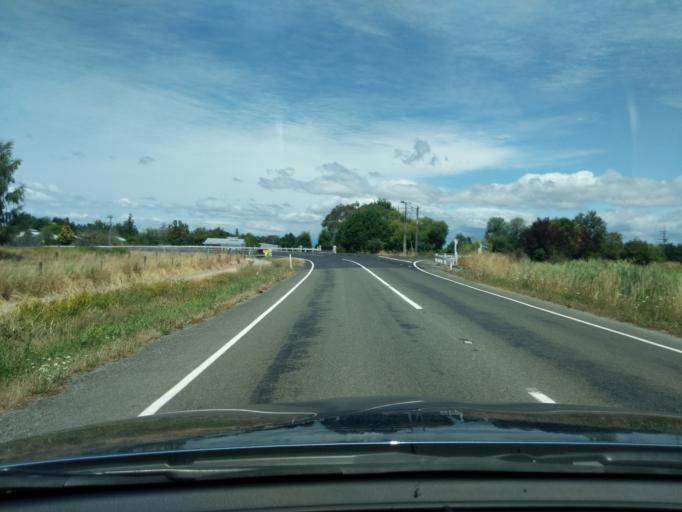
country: NZ
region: Tasman
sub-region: Tasman District
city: Motueka
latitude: -41.0749
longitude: 172.9953
